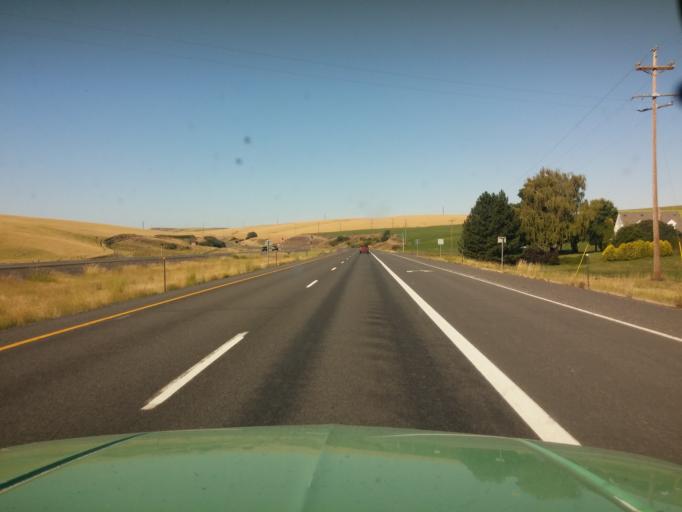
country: US
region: Idaho
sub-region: Nez Perce County
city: Lewiston
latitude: 46.4900
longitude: -117.0240
